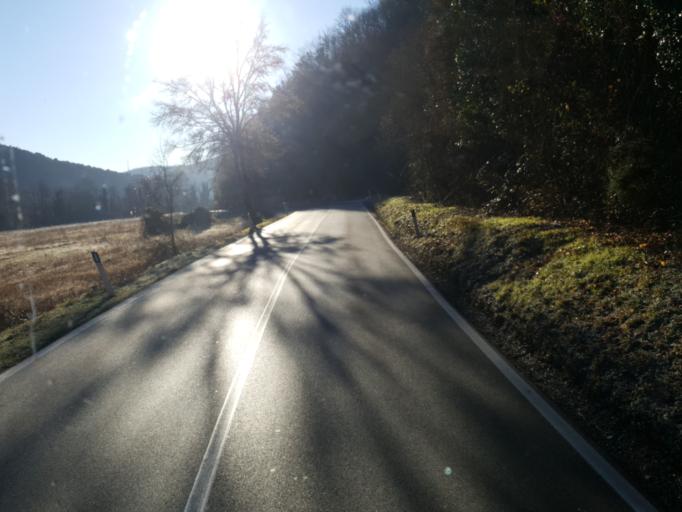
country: IT
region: Latium
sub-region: Provincia di Rieti
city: Colli sul Velino
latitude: 42.5192
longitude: 12.7352
